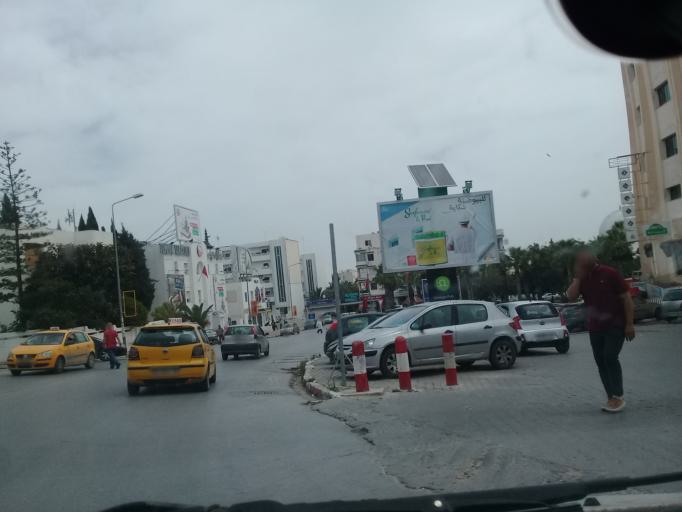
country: TN
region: Tunis
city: Tunis
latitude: 36.8381
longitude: 10.1558
